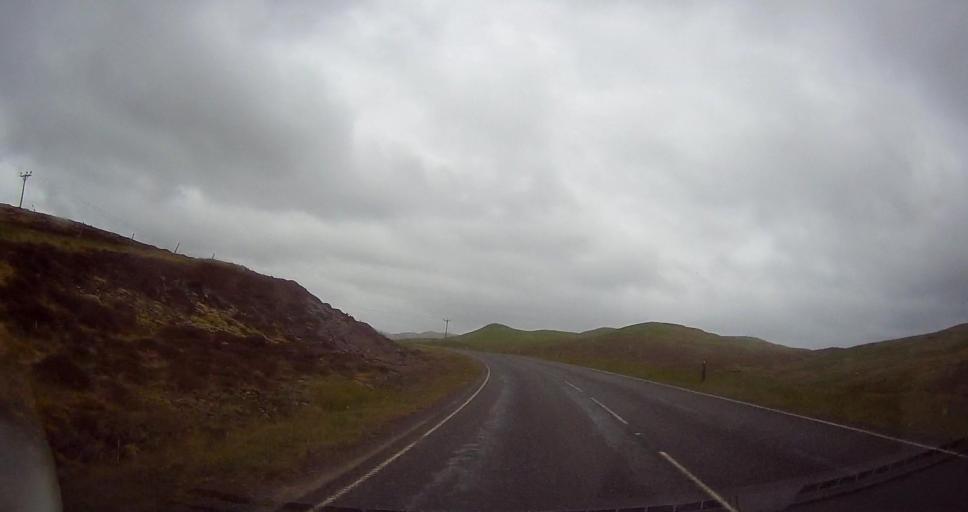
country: GB
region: Scotland
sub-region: Shetland Islands
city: Lerwick
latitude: 60.4350
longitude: -1.3980
